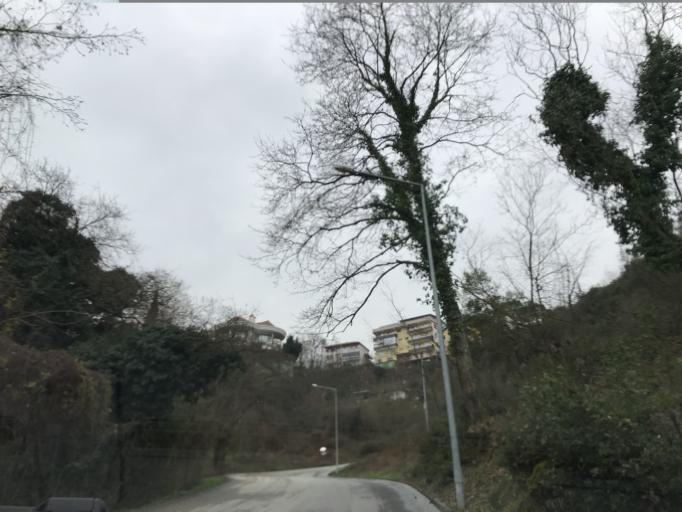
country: TR
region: Yalova
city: Termal
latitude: 40.6012
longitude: 29.1756
